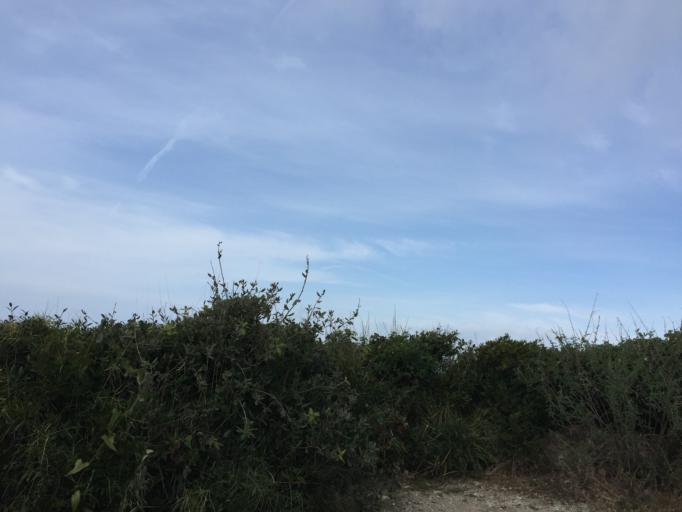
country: IT
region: Campania
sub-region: Provincia di Napoli
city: Monterusciello
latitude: 40.8451
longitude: 14.0489
